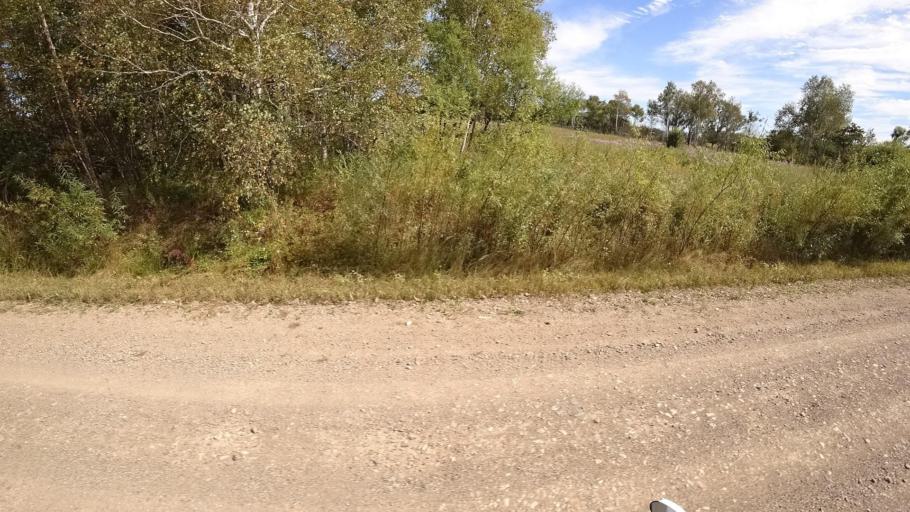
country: RU
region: Primorskiy
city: Yakovlevka
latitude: 44.7165
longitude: 133.6179
